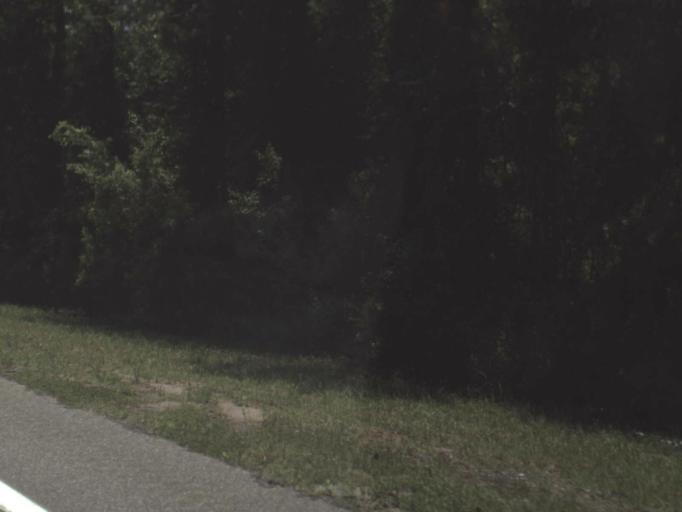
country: US
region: Florida
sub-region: Suwannee County
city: Wellborn
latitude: 30.2173
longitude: -82.8181
